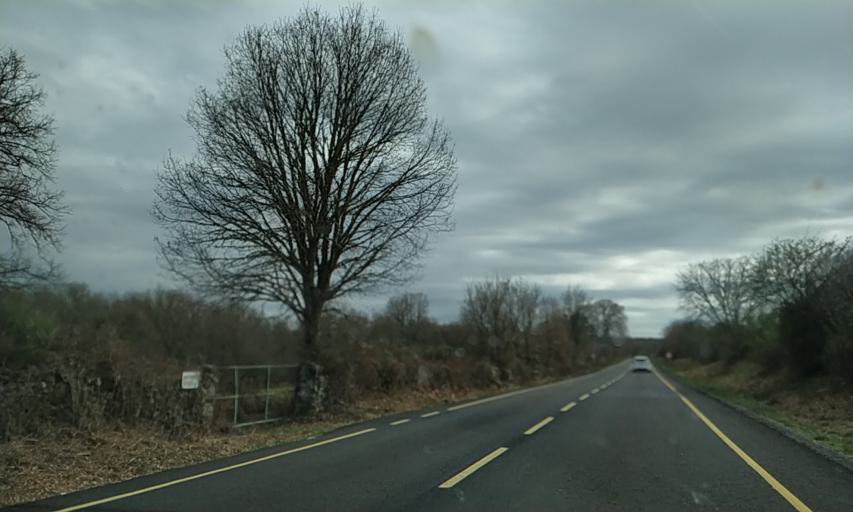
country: ES
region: Castille and Leon
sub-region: Provincia de Salamanca
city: Penaparda
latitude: 40.2776
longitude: -6.6785
